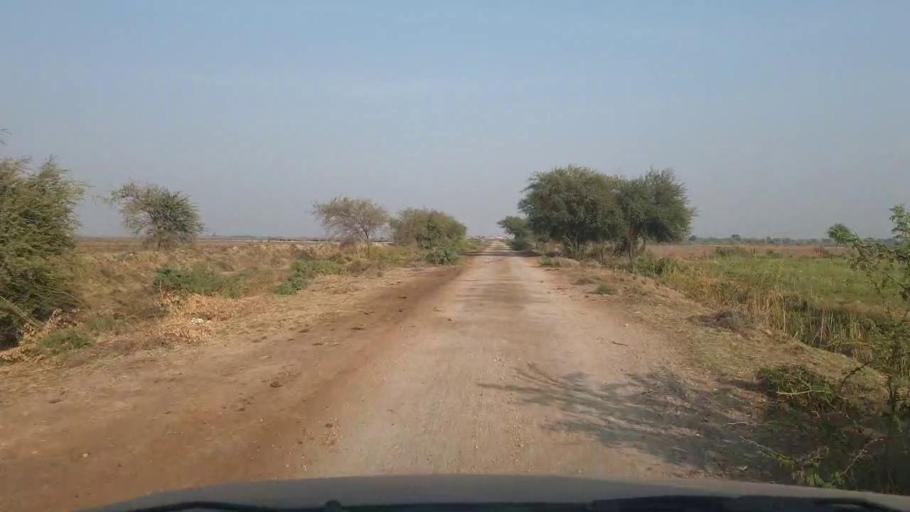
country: PK
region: Sindh
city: Mirwah Gorchani
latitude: 25.2949
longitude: 69.1717
